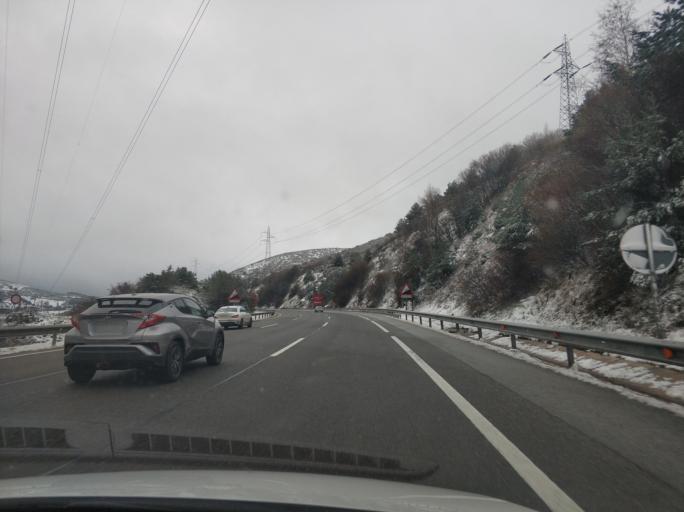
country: ES
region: Madrid
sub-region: Provincia de Madrid
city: Somosierra
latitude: 41.1576
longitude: -3.5853
